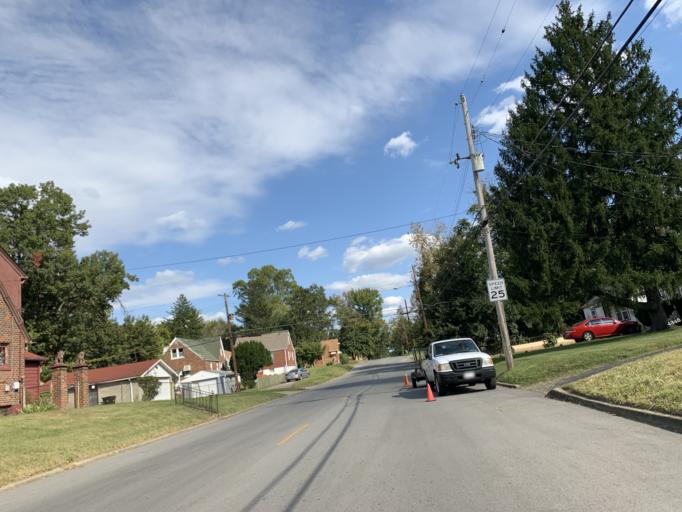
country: US
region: Indiana
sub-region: Floyd County
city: New Albany
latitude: 38.2473
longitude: -85.8252
